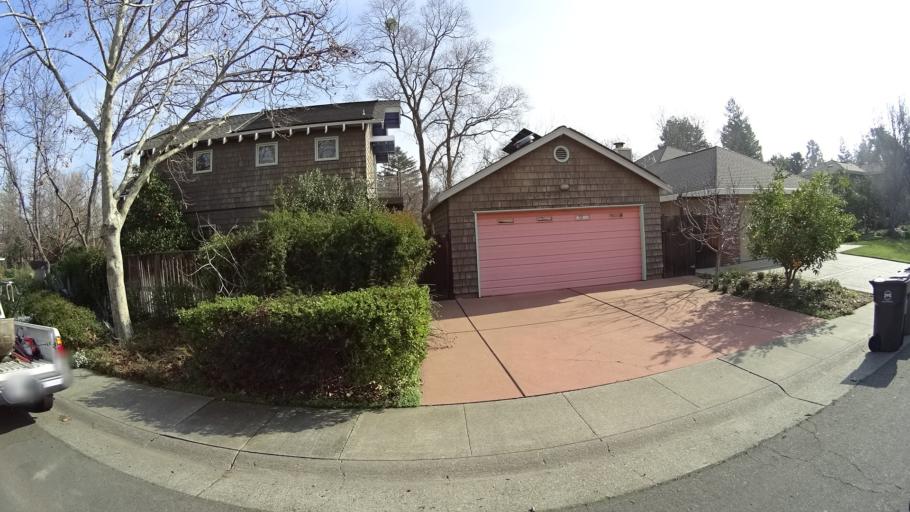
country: US
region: California
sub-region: Yolo County
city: Davis
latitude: 38.5654
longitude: -121.7620
